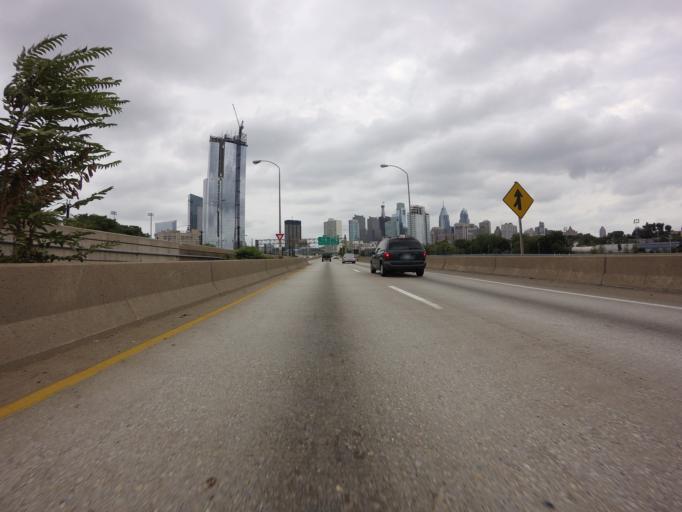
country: US
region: Pennsylvania
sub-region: Philadelphia County
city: Philadelphia
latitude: 39.9481
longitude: -75.1863
